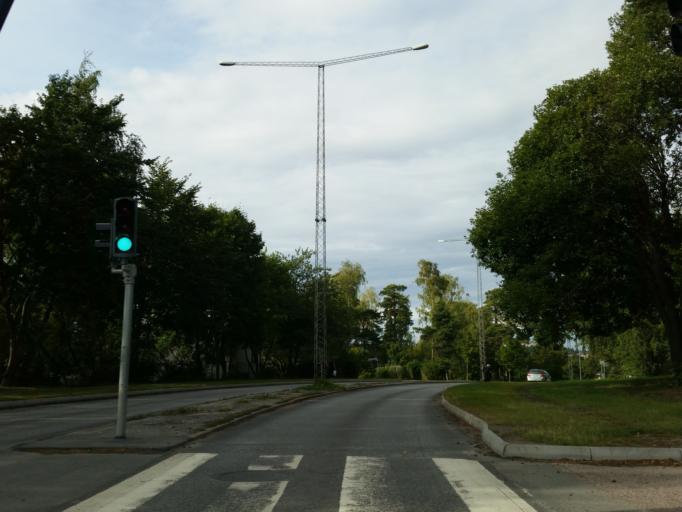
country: SE
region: Stockholm
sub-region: Sollentuna Kommun
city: Sollentuna
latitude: 59.4324
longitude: 17.9495
